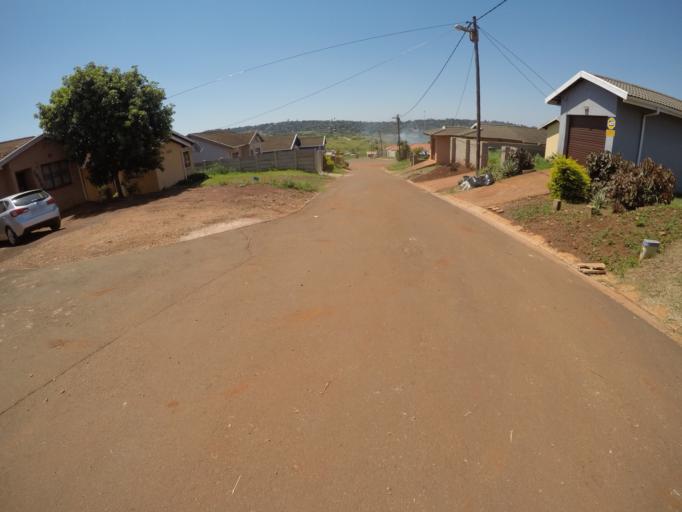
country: ZA
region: KwaZulu-Natal
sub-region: uThungulu District Municipality
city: Empangeni
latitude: -28.7724
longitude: 31.8809
